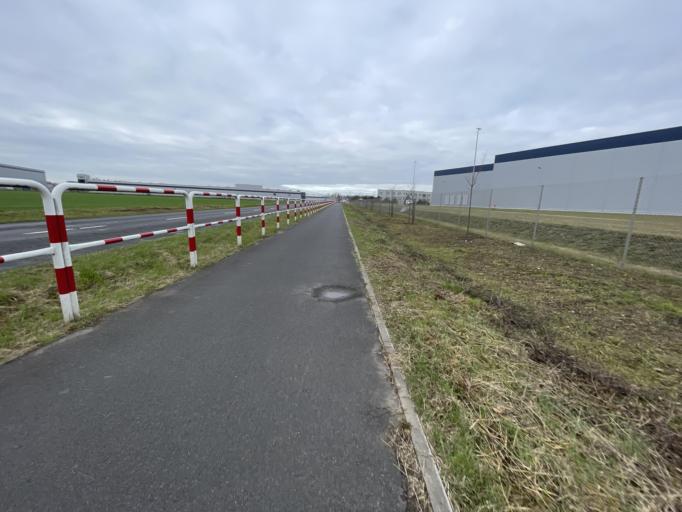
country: PL
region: Greater Poland Voivodeship
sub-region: Powiat poznanski
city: Komorniki
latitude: 52.3427
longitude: 16.7852
